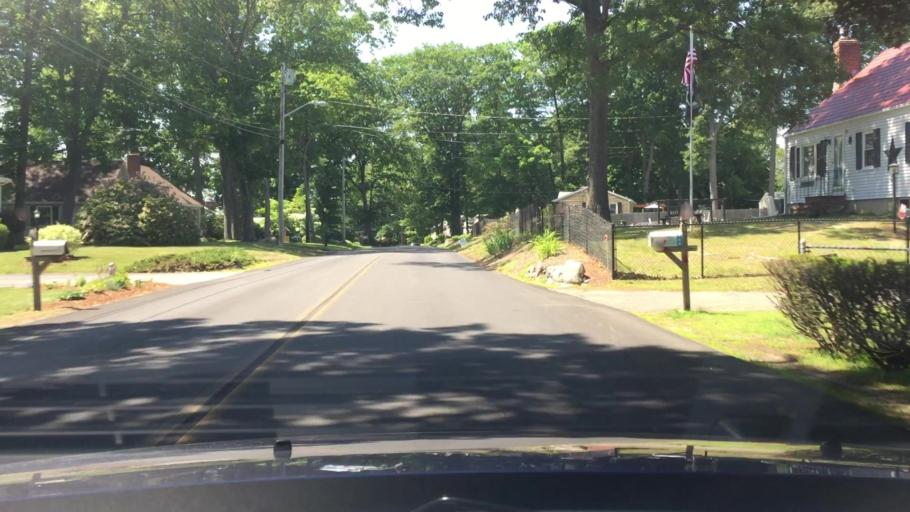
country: US
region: New Hampshire
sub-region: Rockingham County
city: Plaistow
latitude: 42.8193
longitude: -71.0973
